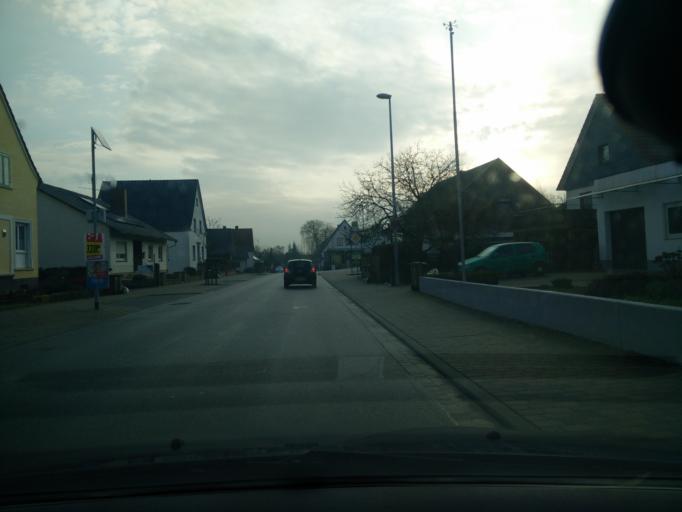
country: DE
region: Rheinland-Pfalz
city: Winden
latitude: 49.0985
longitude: 8.1197
